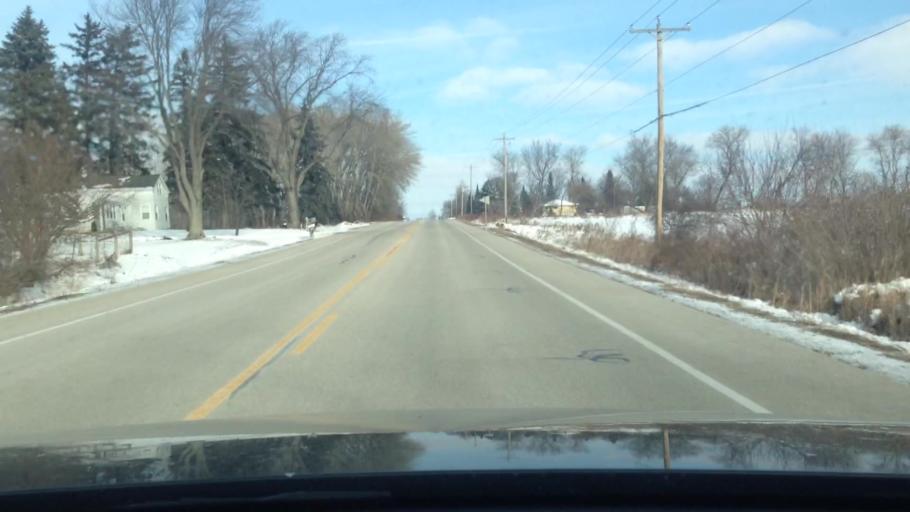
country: US
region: Wisconsin
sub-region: Walworth County
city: Lake Geneva
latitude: 42.6605
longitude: -88.4137
